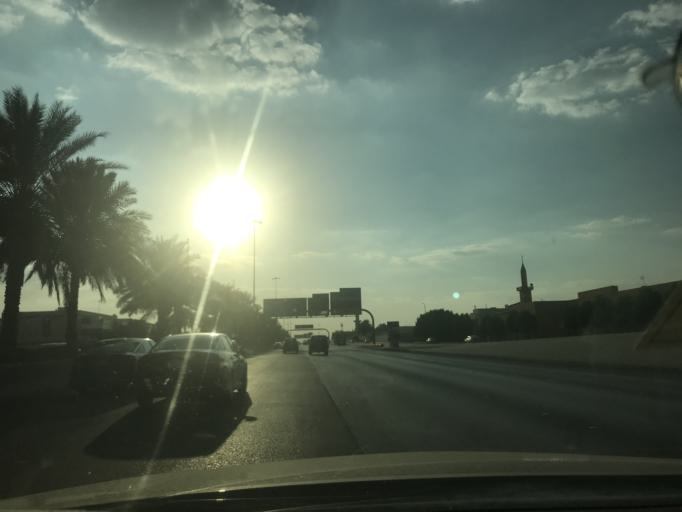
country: SA
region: Ar Riyad
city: Riyadh
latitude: 24.7419
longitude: 46.6016
